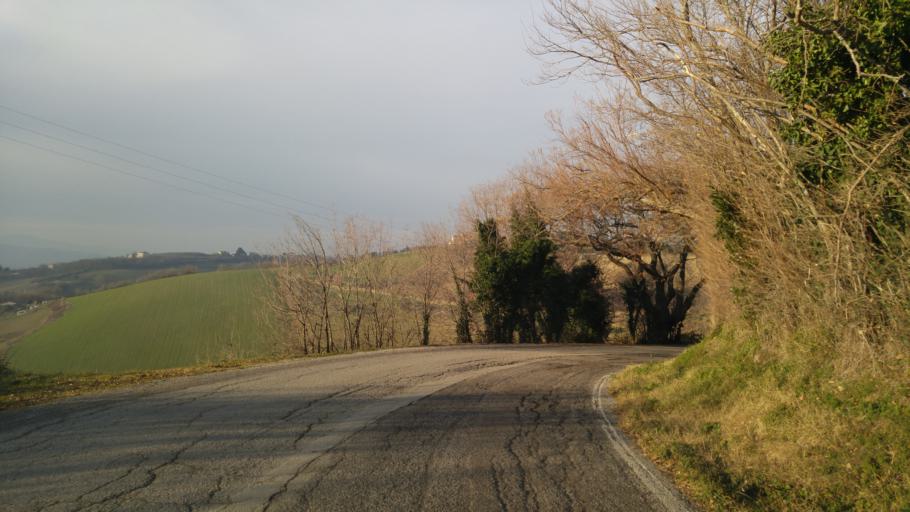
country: IT
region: The Marches
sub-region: Provincia di Pesaro e Urbino
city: Piagge
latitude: 43.7329
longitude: 12.9655
